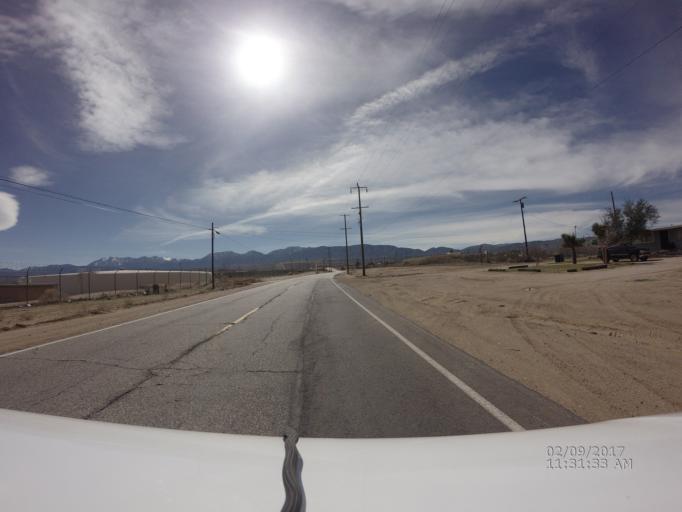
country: US
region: California
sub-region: Los Angeles County
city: Littlerock
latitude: 34.5249
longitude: -117.9228
